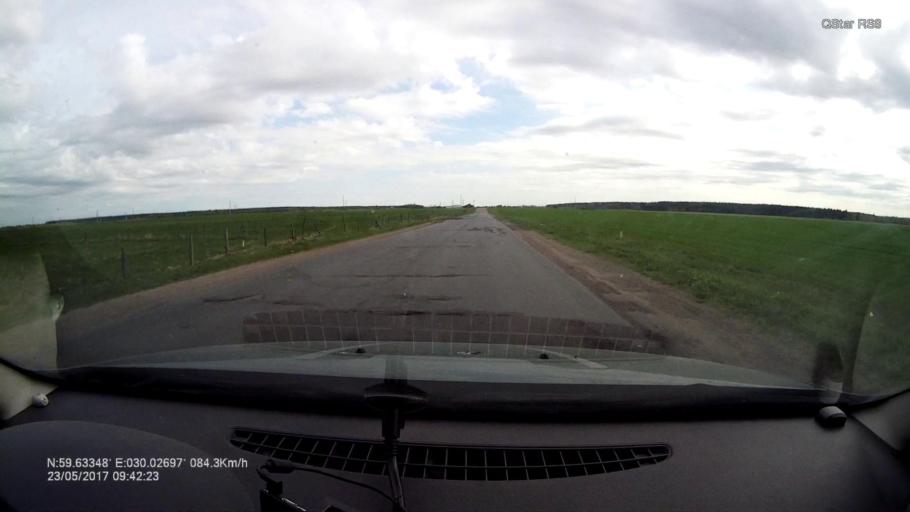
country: RU
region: Leningrad
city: Mariyenburg
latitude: 59.6336
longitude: 30.0273
